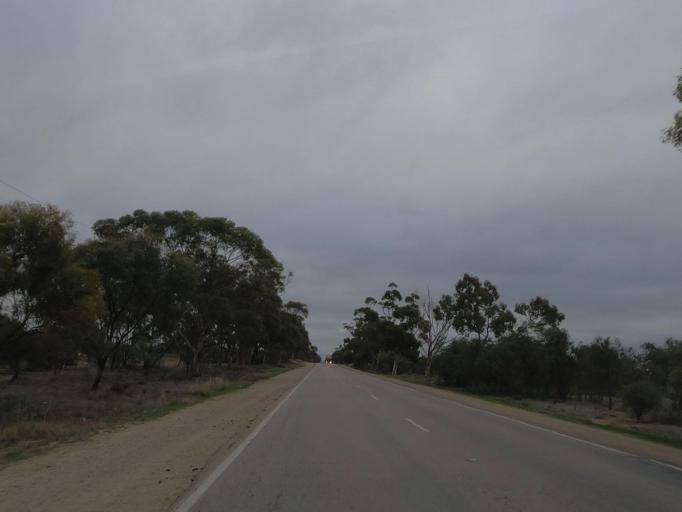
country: AU
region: Victoria
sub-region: Swan Hill
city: Swan Hill
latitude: -35.4080
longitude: 143.5831
